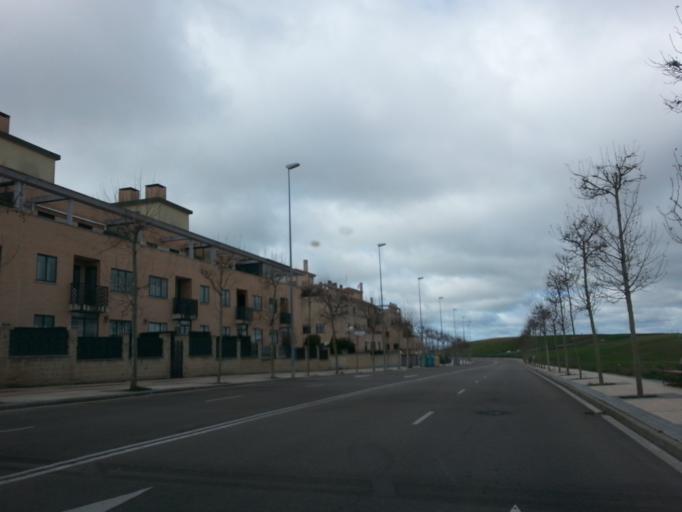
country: ES
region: Castille and Leon
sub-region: Provincia de Salamanca
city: Salamanca
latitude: 40.9816
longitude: -5.6723
